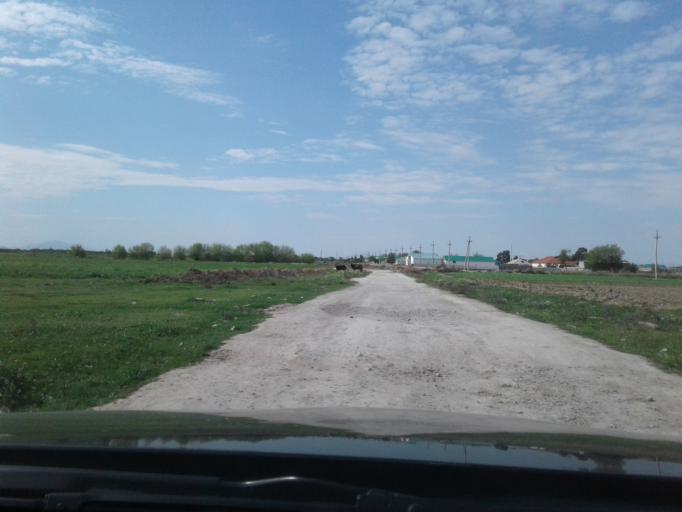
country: TM
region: Ahal
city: Ashgabat
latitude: 37.9794
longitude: 58.2906
